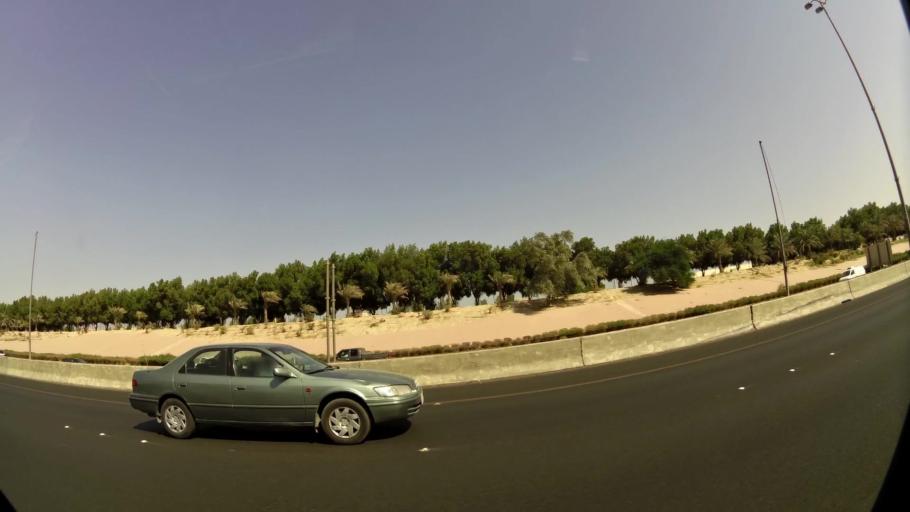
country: KW
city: Bayan
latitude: 29.2998
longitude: 48.0251
